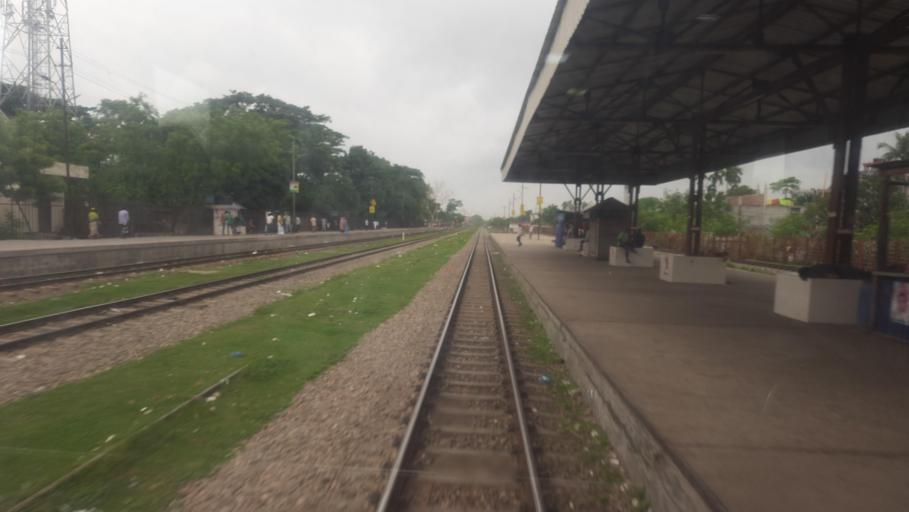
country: BD
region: Dhaka
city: Narsingdi
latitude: 23.9311
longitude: 90.7207
